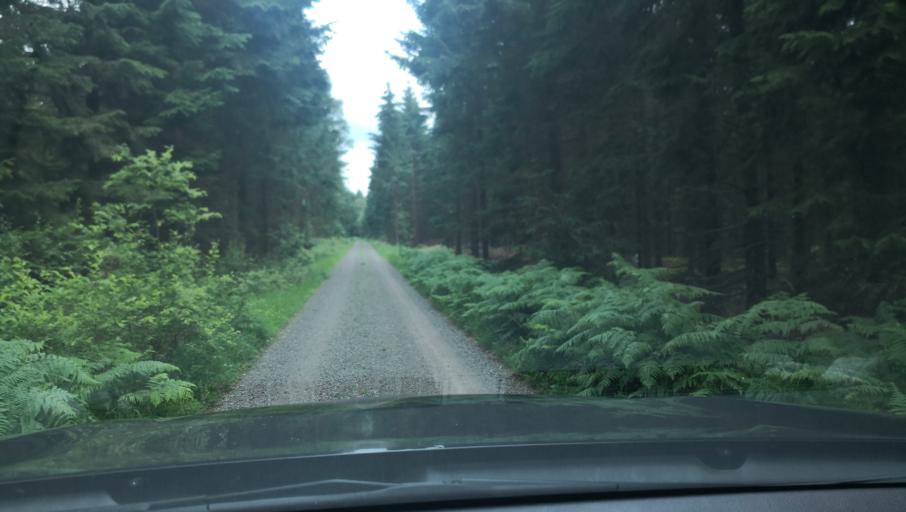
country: SE
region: Skane
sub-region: Simrishamns Kommun
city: Kivik
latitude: 55.6093
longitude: 14.1198
